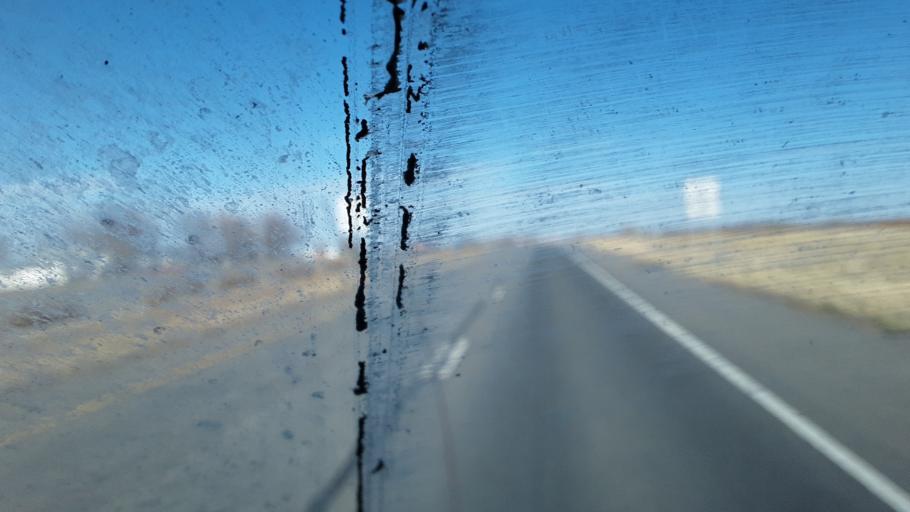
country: US
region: Colorado
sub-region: Weld County
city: Hudson
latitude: 40.0550
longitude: -104.6608
